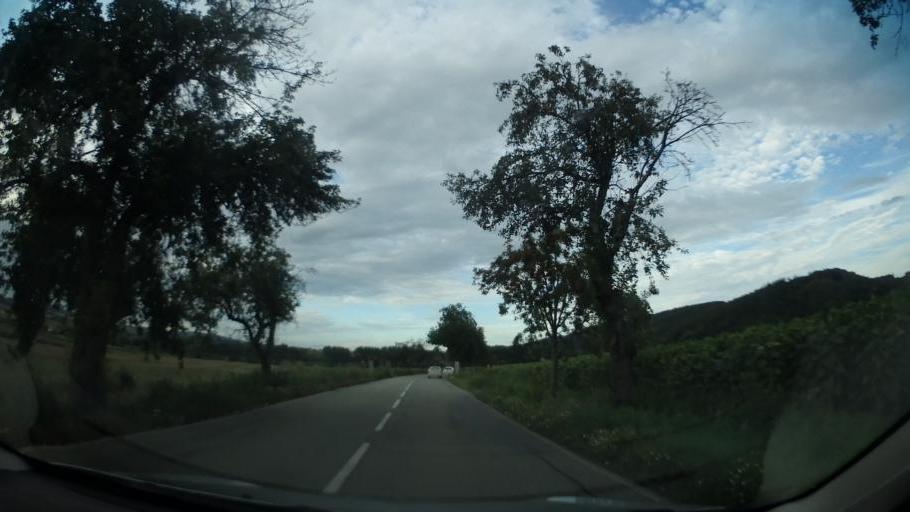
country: CZ
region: South Moravian
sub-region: Okres Blansko
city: Boskovice
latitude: 49.5095
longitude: 16.6716
